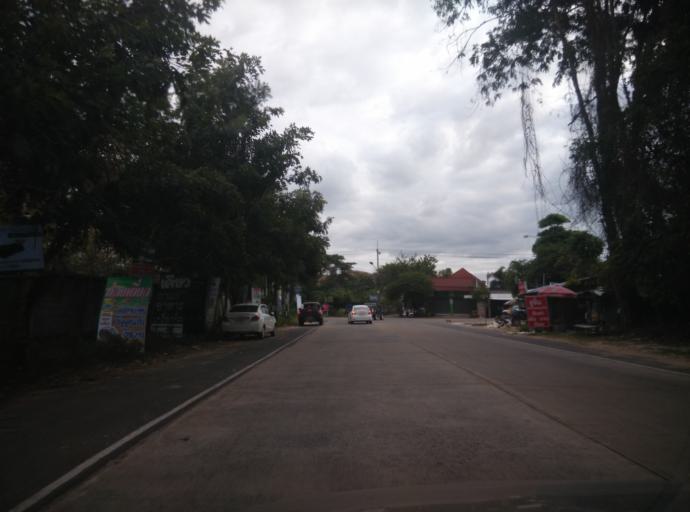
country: TH
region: Sisaket
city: Si Sa Ket
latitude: 15.1158
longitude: 104.3556
